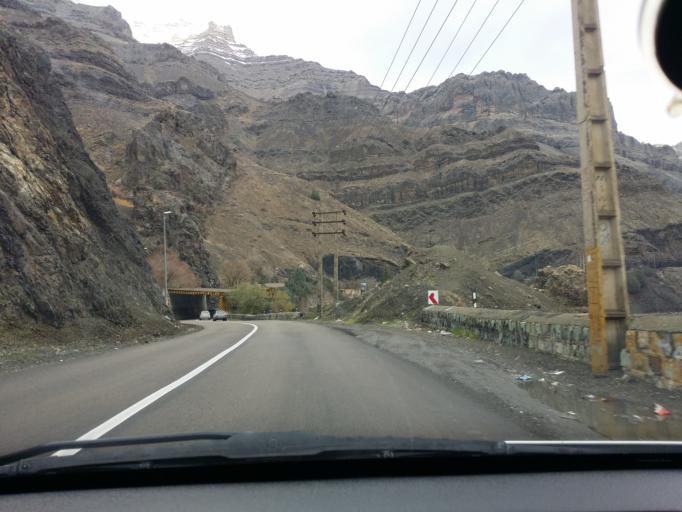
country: IR
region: Alborz
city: Karaj
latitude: 35.9995
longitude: 51.1139
